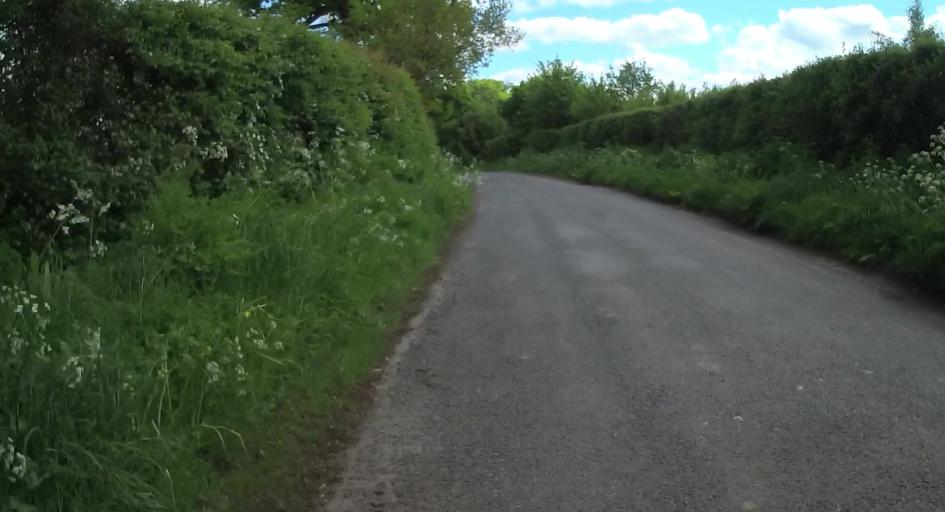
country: GB
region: England
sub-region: West Berkshire
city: Stratfield Mortimer
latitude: 51.3380
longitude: -1.0382
